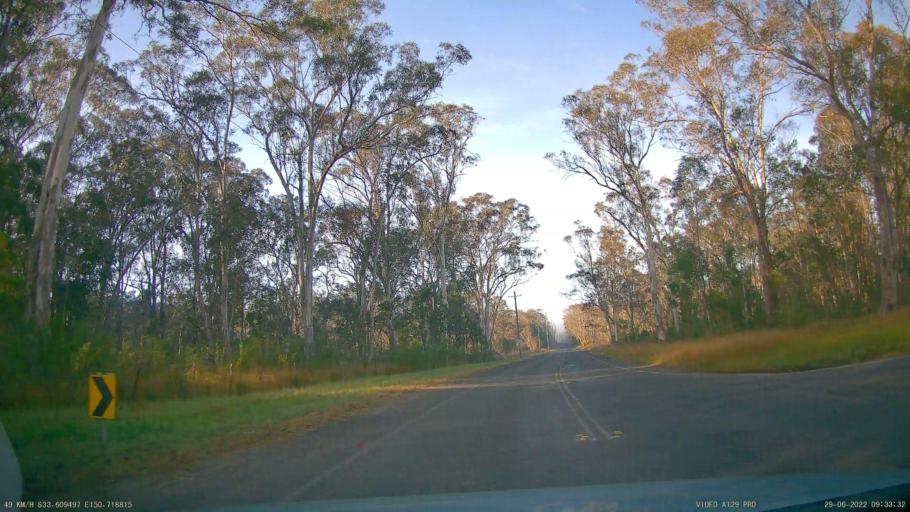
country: AU
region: New South Wales
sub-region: Hawkesbury
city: Richmond
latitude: -33.6100
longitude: 150.7190
